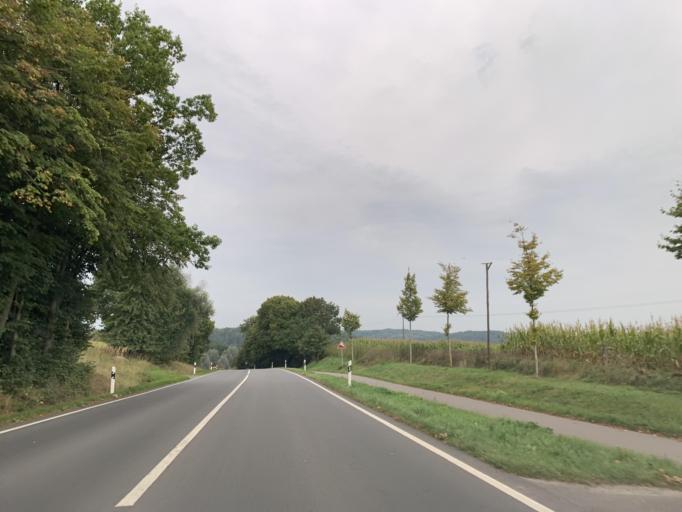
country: DE
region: Mecklenburg-Vorpommern
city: Loitz
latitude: 53.3427
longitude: 13.4695
